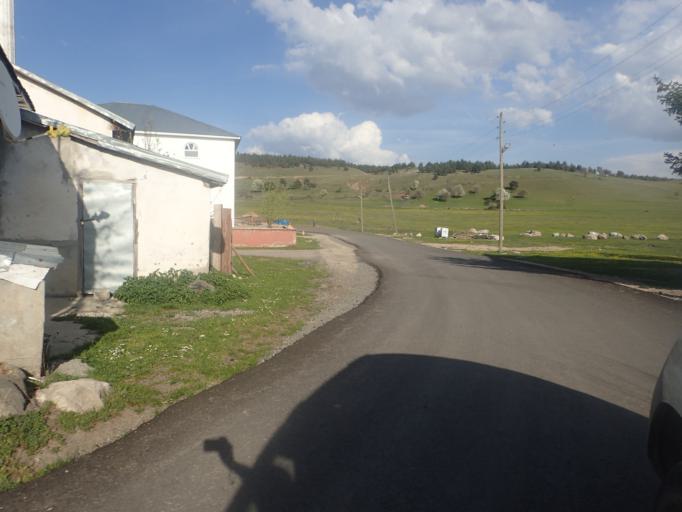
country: TR
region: Ordu
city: Mesudiye
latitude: 40.3995
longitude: 37.8331
